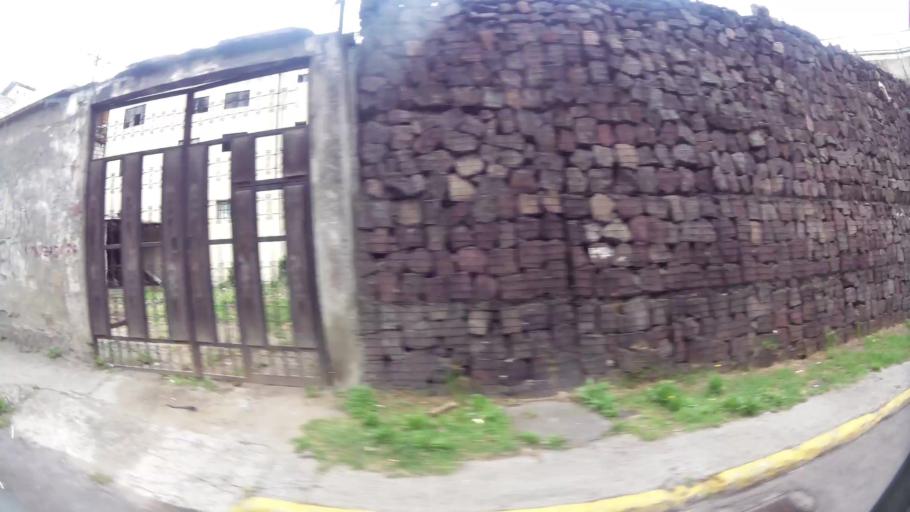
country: EC
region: Pichincha
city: Quito
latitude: -0.2261
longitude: -78.5133
